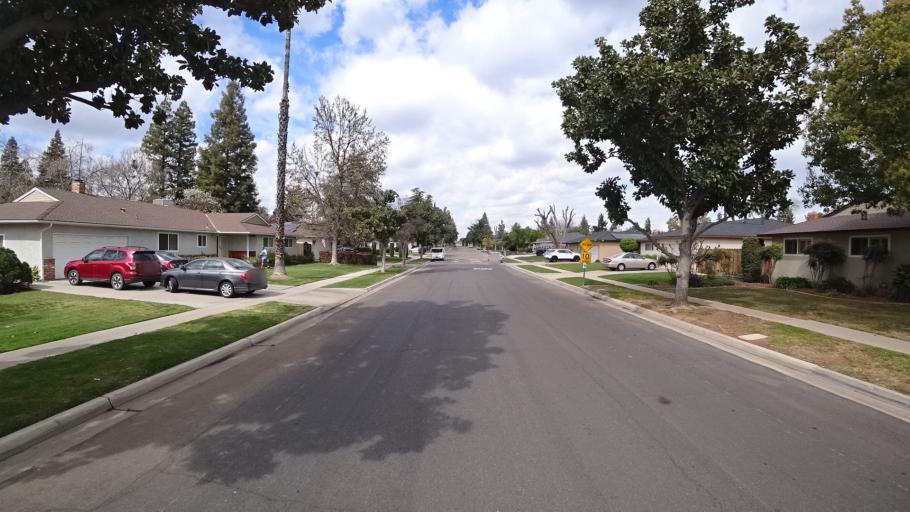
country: US
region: California
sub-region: Fresno County
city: Clovis
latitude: 36.8207
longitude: -119.7672
